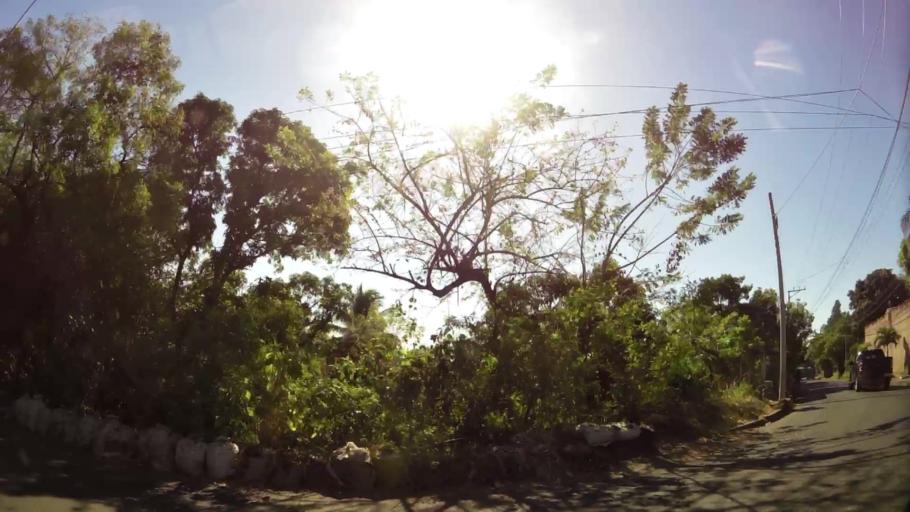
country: SV
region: Sonsonate
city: Sonzacate
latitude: 13.7346
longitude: -89.7193
